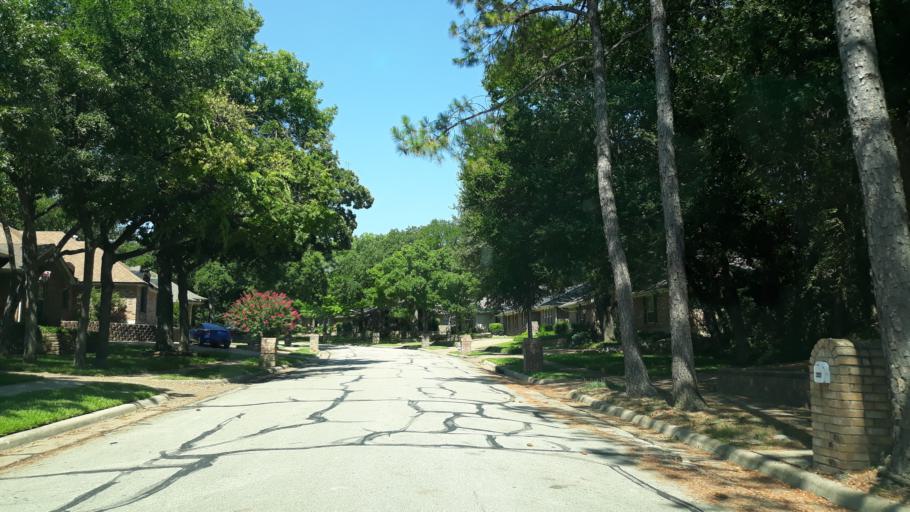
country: US
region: Texas
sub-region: Dallas County
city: Irving
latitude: 32.8253
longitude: -97.0069
